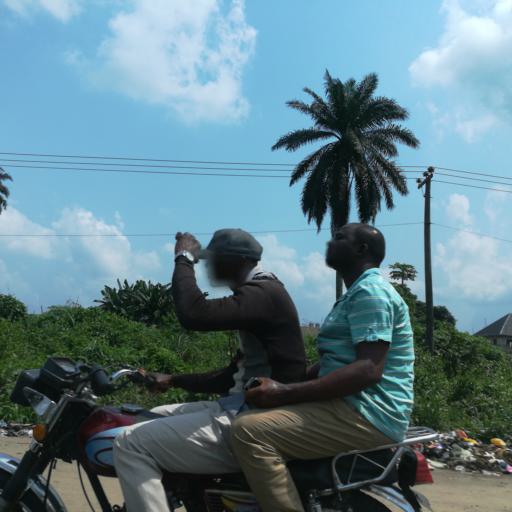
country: NG
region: Rivers
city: Okrika
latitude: 4.8303
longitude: 7.0891
